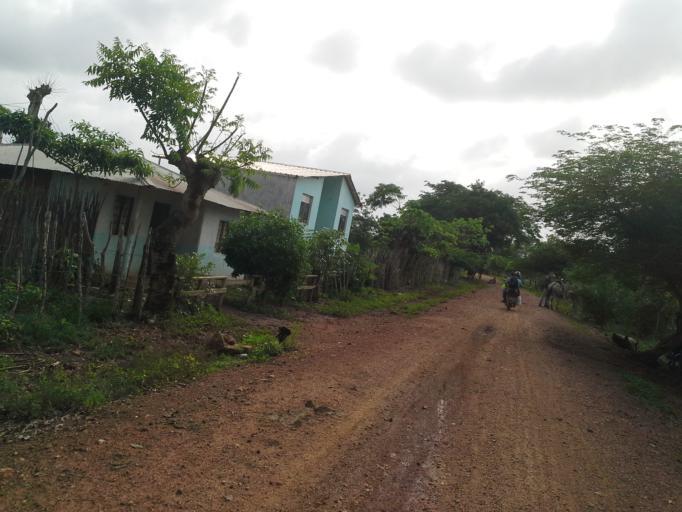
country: CO
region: Cordoba
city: Chima
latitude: 9.1036
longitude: -75.6204
